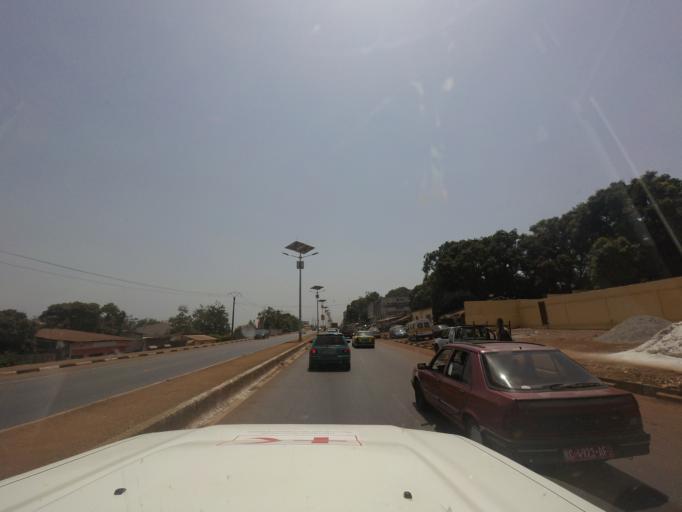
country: GN
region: Conakry
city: Conakry
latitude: 9.6294
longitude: -13.5757
